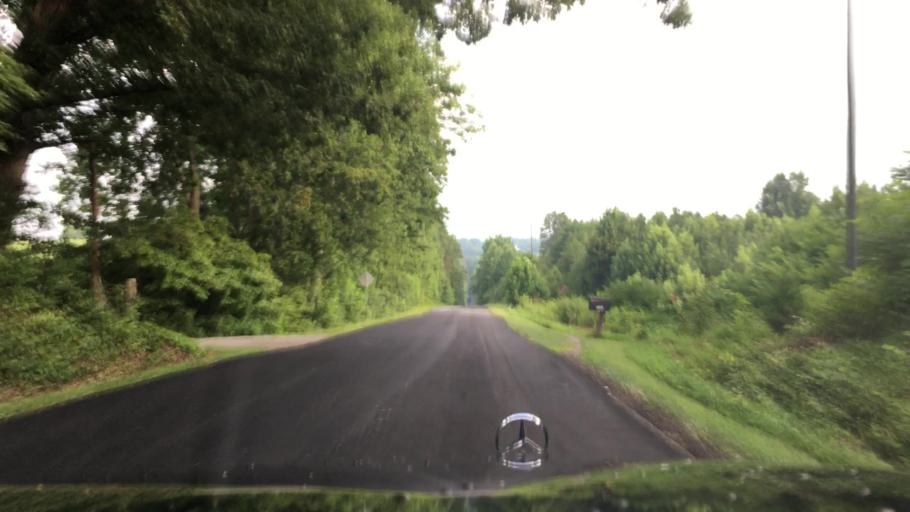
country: US
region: Virginia
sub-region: Campbell County
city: Timberlake
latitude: 37.2428
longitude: -79.3011
